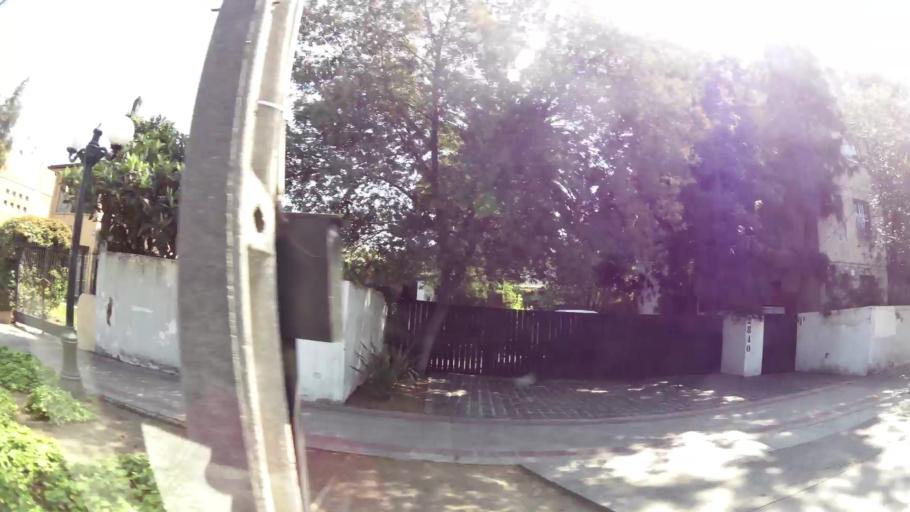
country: CL
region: Santiago Metropolitan
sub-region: Provincia de Santiago
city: Villa Presidente Frei, Nunoa, Santiago, Chile
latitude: -33.4374
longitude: -70.5907
